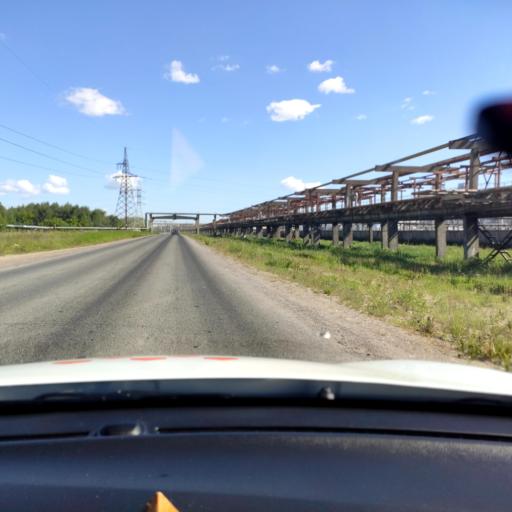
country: RU
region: Tatarstan
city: Staroye Arakchino
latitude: 55.8747
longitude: 48.9747
